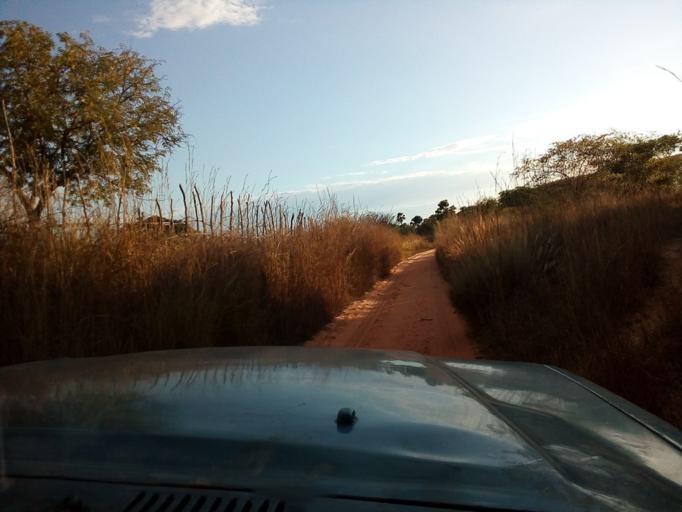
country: MG
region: Boeny
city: Sitampiky
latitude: -16.1261
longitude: 45.5087
